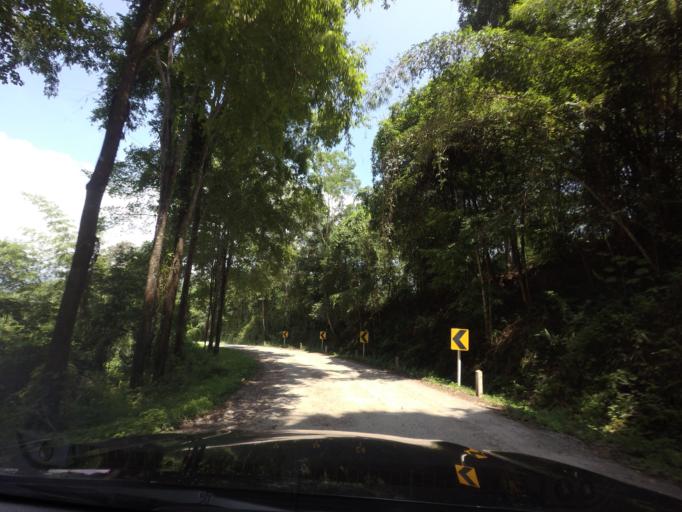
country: TH
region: Loei
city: Na Haeo
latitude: 17.6204
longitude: 100.9005
